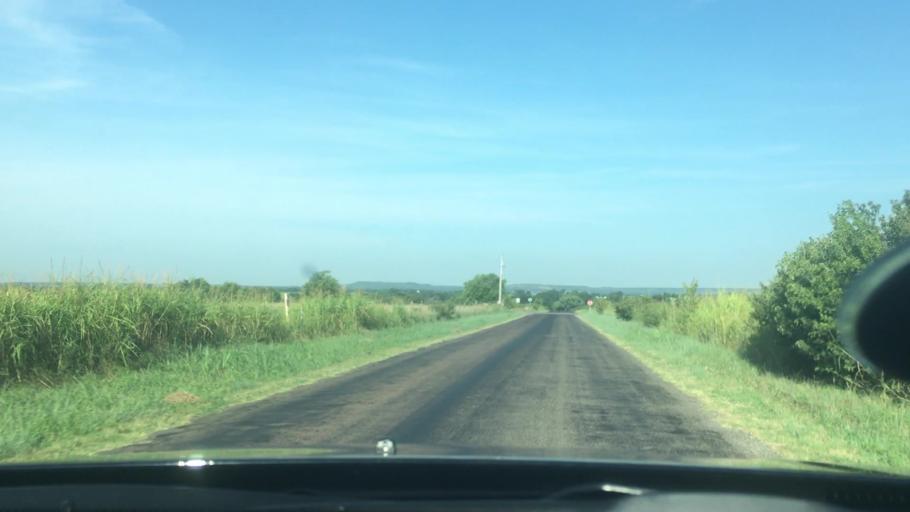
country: US
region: Oklahoma
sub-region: Garvin County
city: Maysville
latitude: 34.6520
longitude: -97.4033
